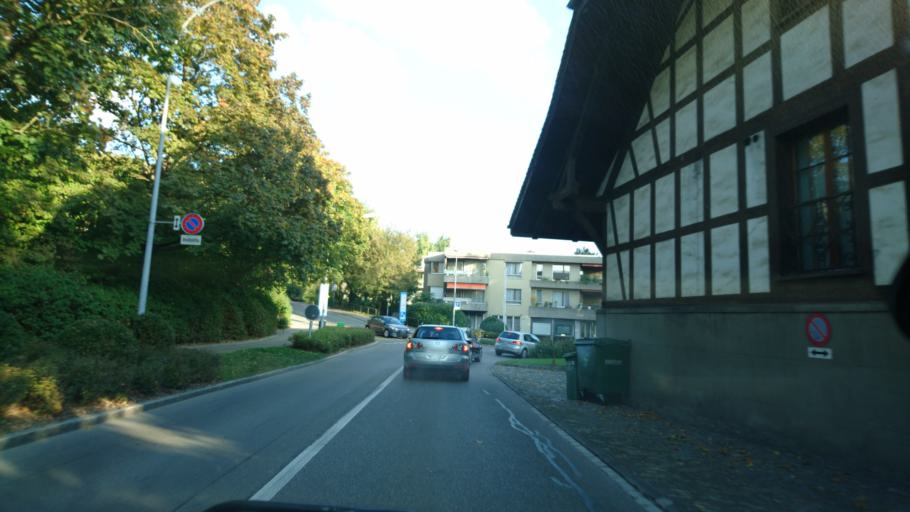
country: CH
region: Bern
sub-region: Bern-Mittelland District
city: Bolligen
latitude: 46.9752
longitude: 7.4841
